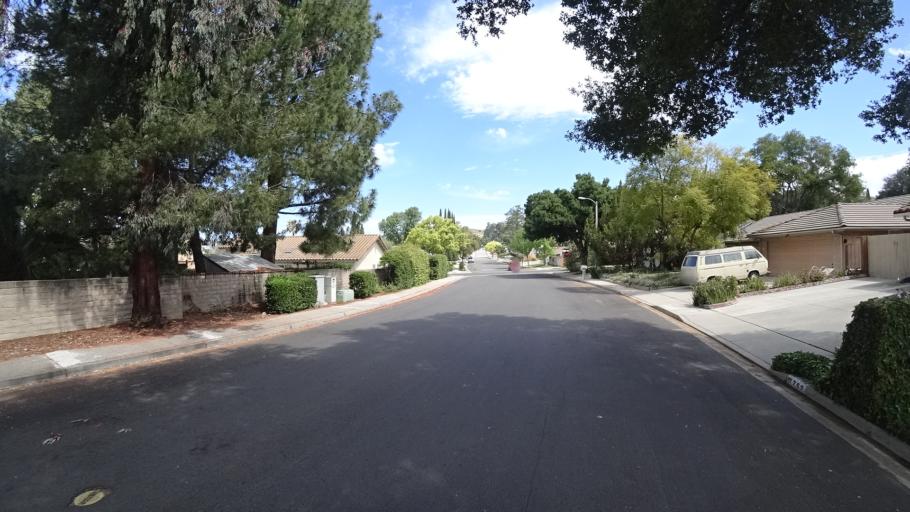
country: US
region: California
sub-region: Ventura County
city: Casa Conejo
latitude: 34.1642
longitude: -118.9405
